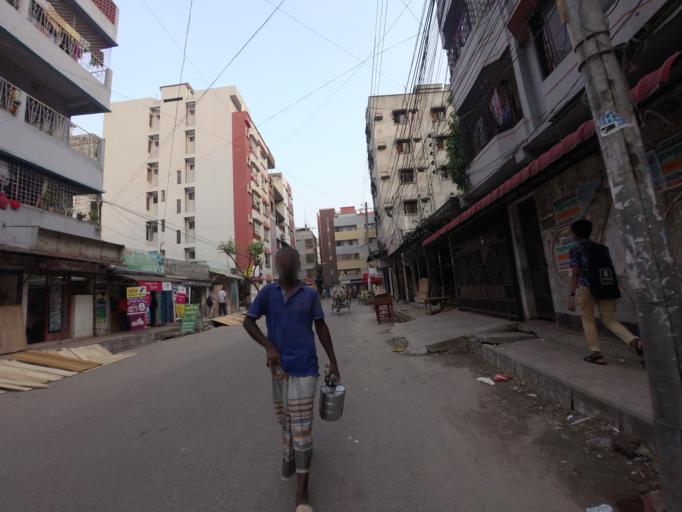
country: BD
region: Dhaka
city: Azimpur
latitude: 23.7690
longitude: 90.3623
